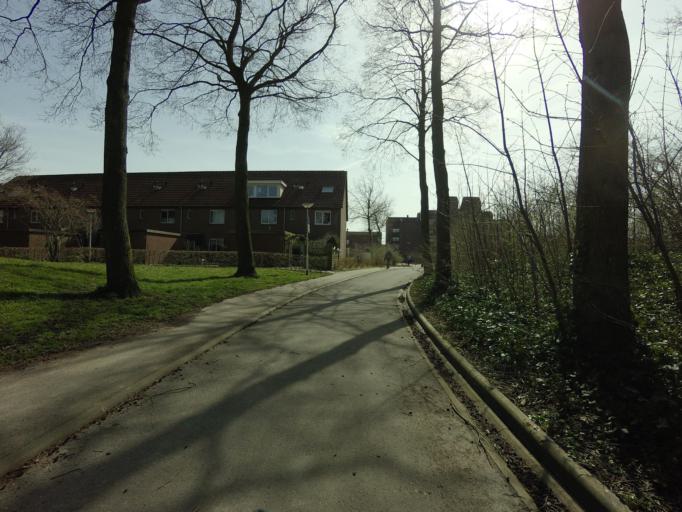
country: NL
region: South Holland
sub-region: Gemeente Zoetermeer
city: Zoetermeer
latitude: 52.0738
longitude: 4.5098
